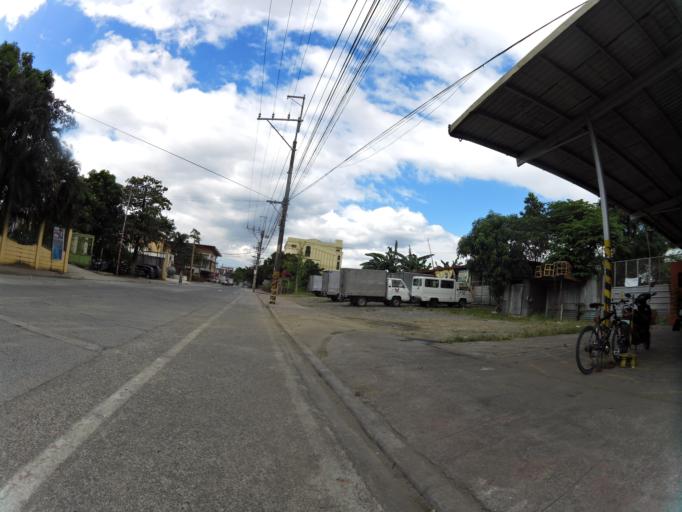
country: PH
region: Calabarzon
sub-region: Province of Rizal
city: Antipolo
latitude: 14.6388
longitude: 121.1112
